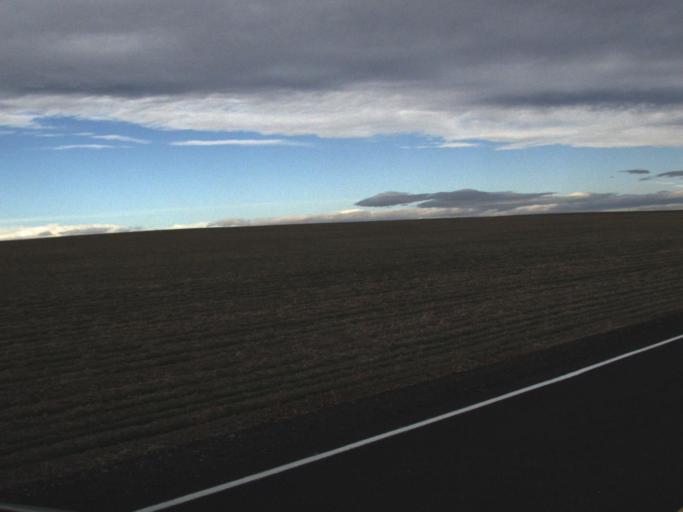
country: US
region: Washington
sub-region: Okanogan County
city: Coulee Dam
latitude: 47.6241
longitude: -118.7207
